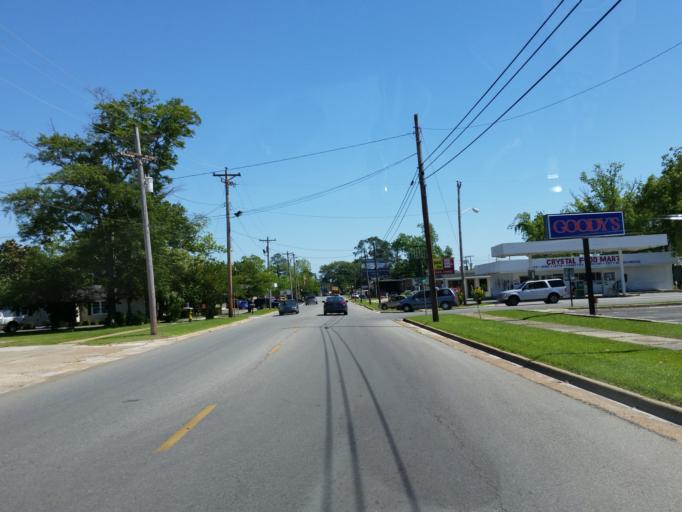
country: US
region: Georgia
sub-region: Cook County
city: Adel
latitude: 31.1413
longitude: -83.4249
